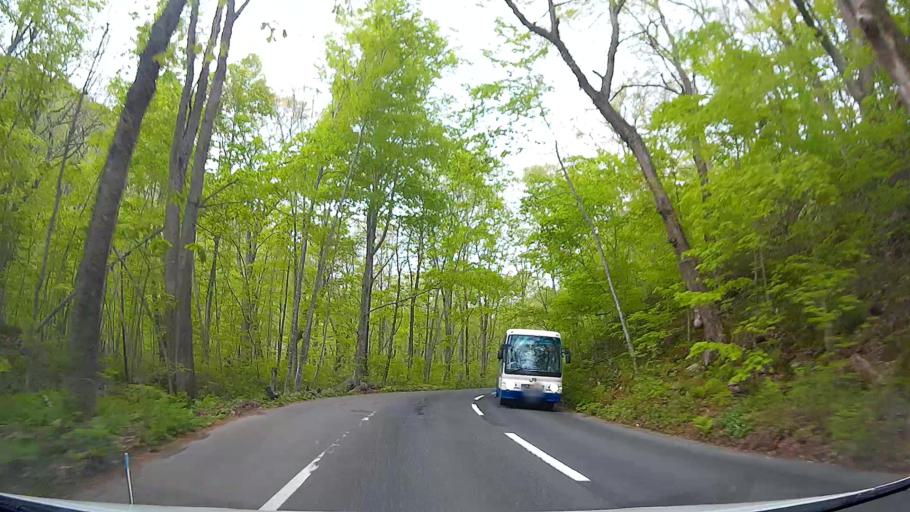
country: JP
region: Aomori
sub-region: Aomori Shi
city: Furudate
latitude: 40.5659
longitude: 140.9744
